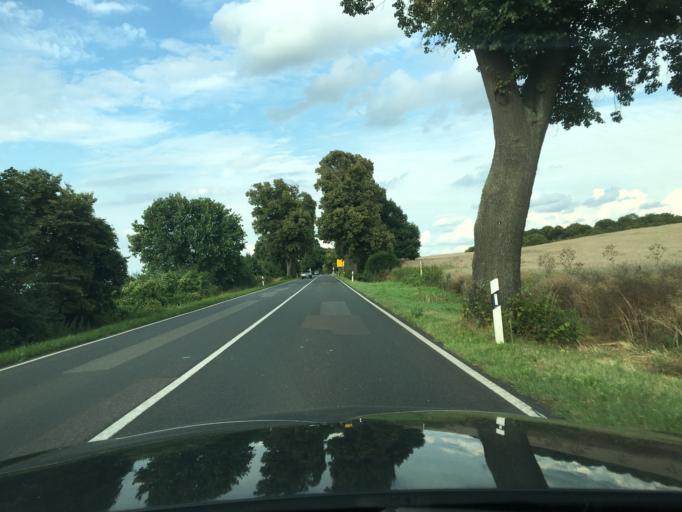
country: DE
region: Mecklenburg-Vorpommern
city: Wustrow
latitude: 53.4279
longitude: 13.1484
